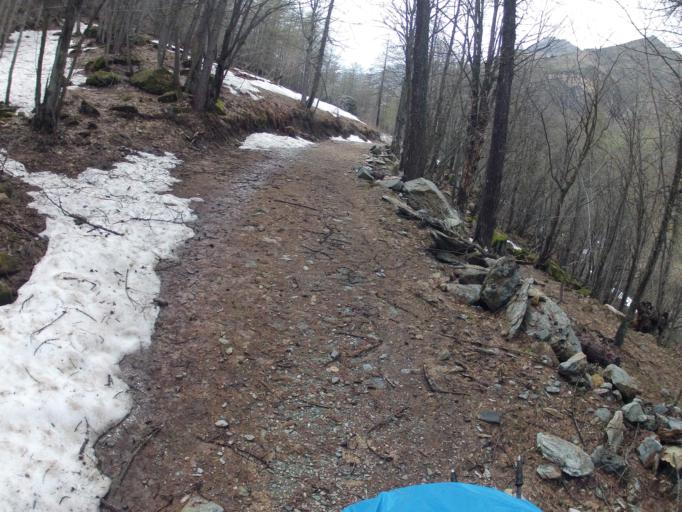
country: IT
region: Piedmont
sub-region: Provincia di Cuneo
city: Crissolo
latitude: 44.7012
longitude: 7.1417
